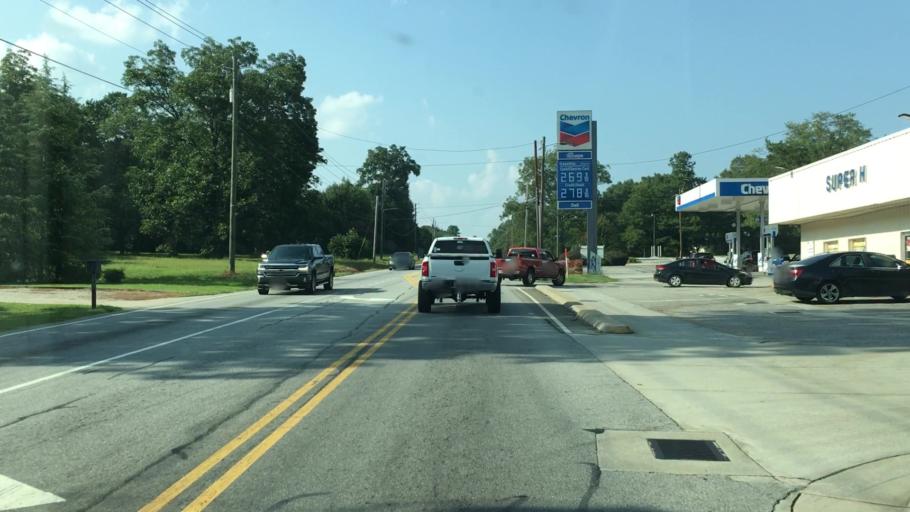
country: US
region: Georgia
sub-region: Barrow County
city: Russell
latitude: 33.9326
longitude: -83.7141
